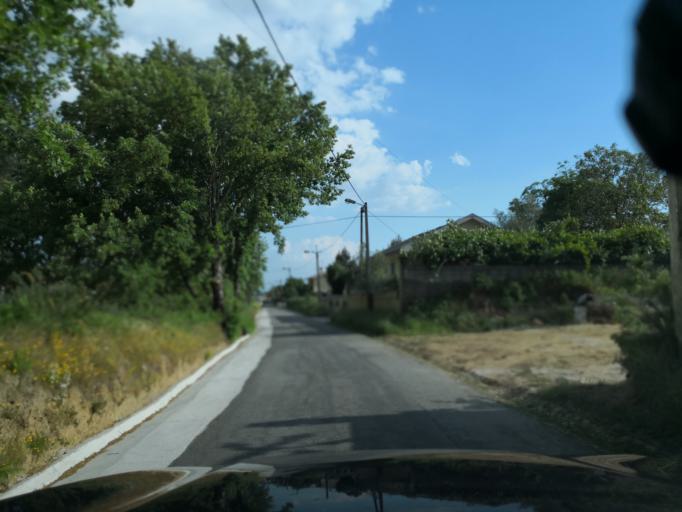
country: PT
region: Vila Real
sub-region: Vila Real
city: Vila Real
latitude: 41.3488
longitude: -7.7236
